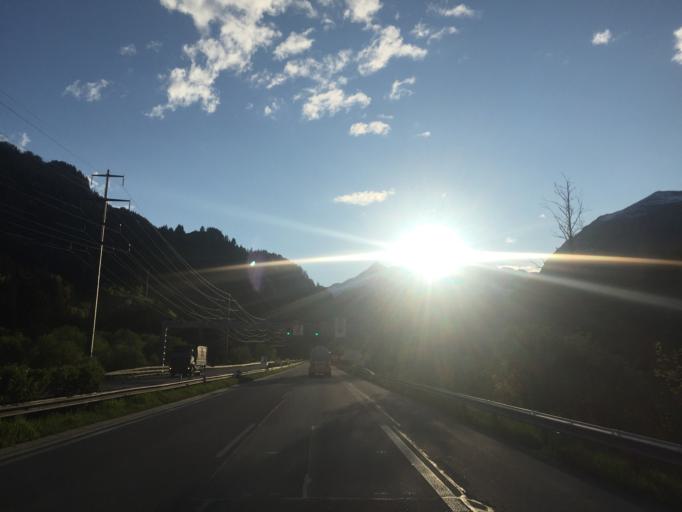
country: CH
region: Ticino
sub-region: Leventina District
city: Airolo
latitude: 46.5195
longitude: 8.6446
